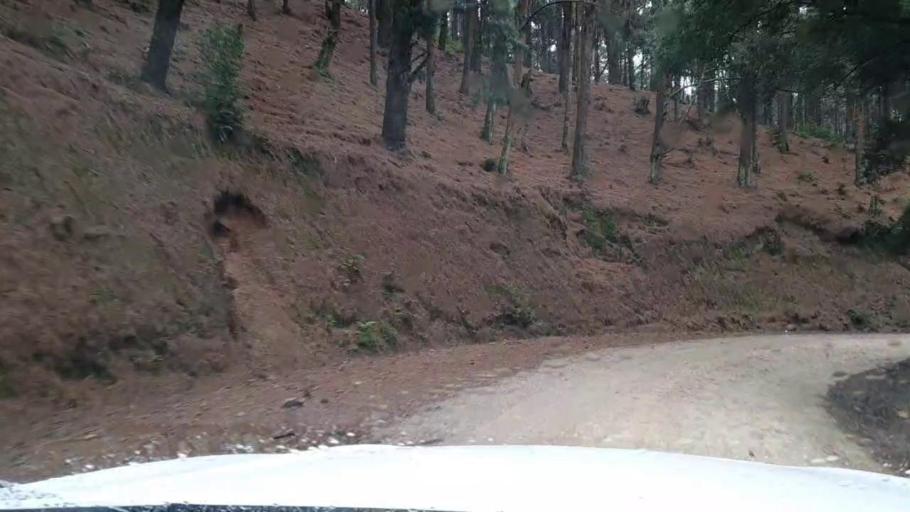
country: RW
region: Southern Province
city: Nzega
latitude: -2.3654
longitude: 29.3776
